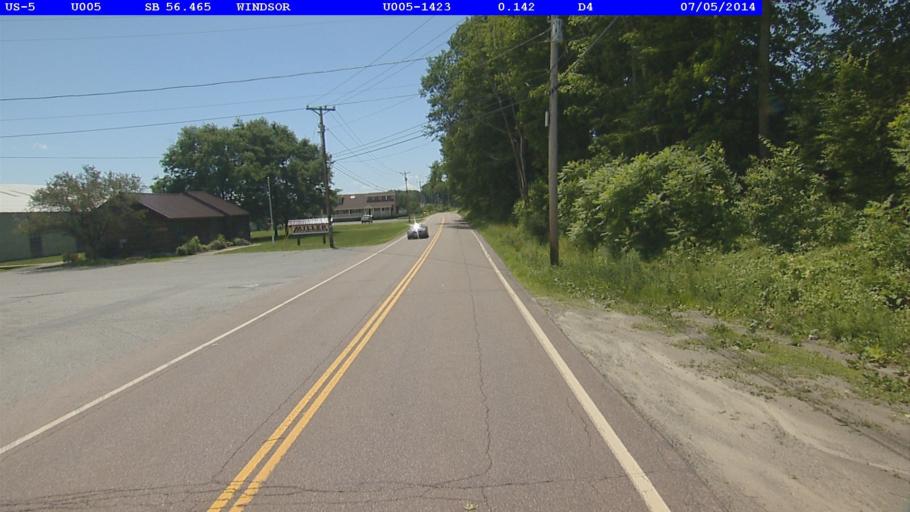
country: US
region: Vermont
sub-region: Windsor County
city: Windsor
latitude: 43.4310
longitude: -72.3981
